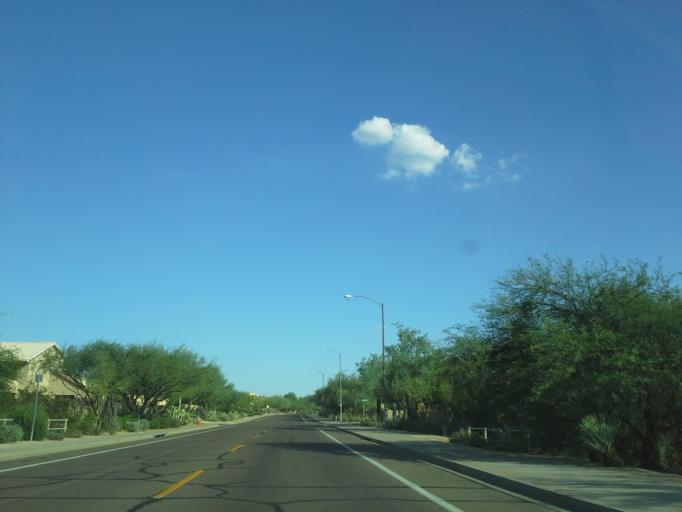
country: US
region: Arizona
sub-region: Maricopa County
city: Cave Creek
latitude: 33.7647
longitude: -111.9925
